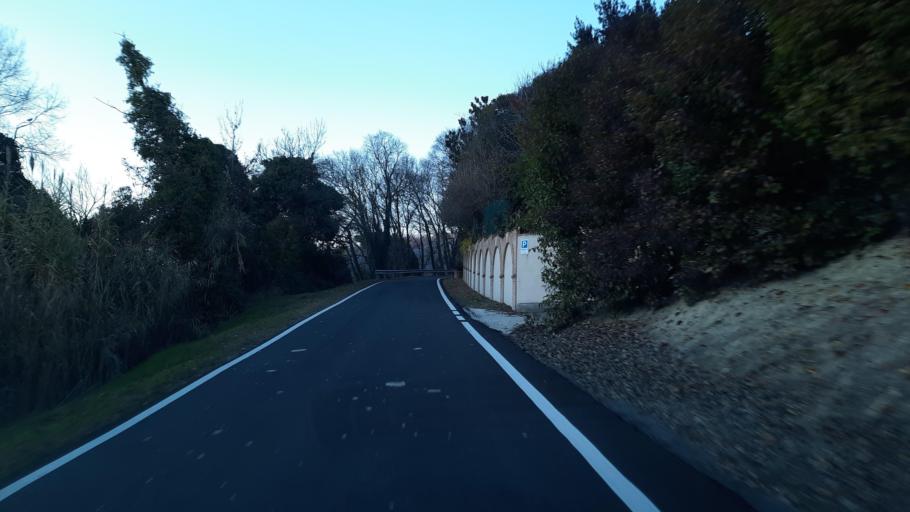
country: IT
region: Piedmont
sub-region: Provincia di Alessandria
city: Mombello Monferrato
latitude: 45.1551
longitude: 8.2593
